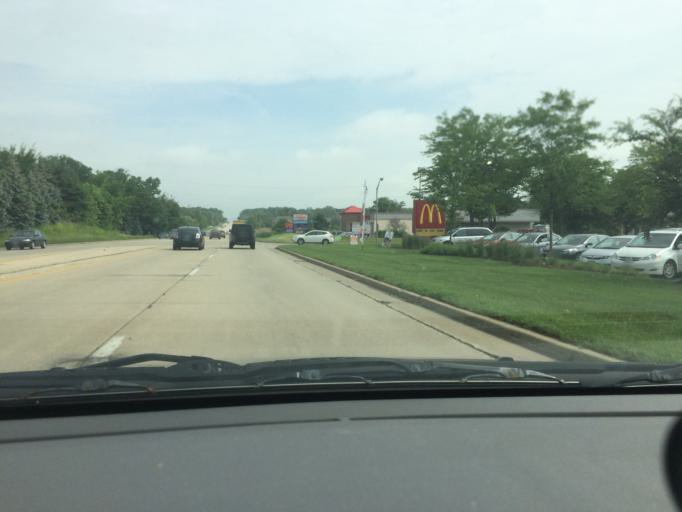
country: US
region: Illinois
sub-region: Cook County
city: Bartlett
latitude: 41.9776
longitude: -88.2070
